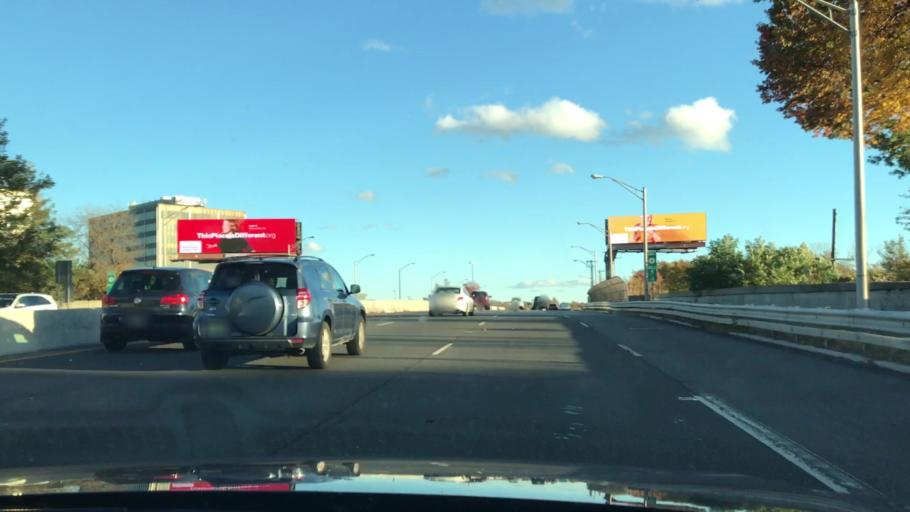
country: US
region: New Jersey
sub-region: Bergen County
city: River Edge
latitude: 40.9094
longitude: -74.0370
